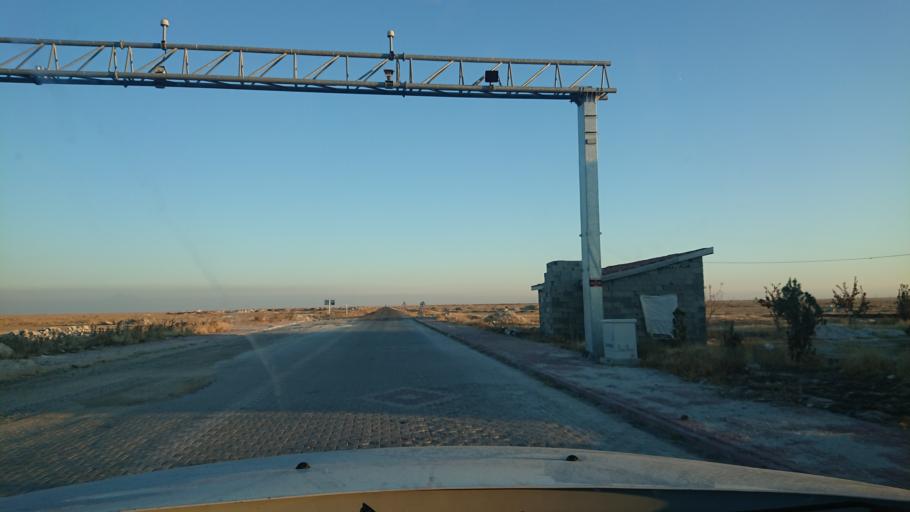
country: TR
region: Aksaray
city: Eskil
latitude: 38.3934
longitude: 33.4264
